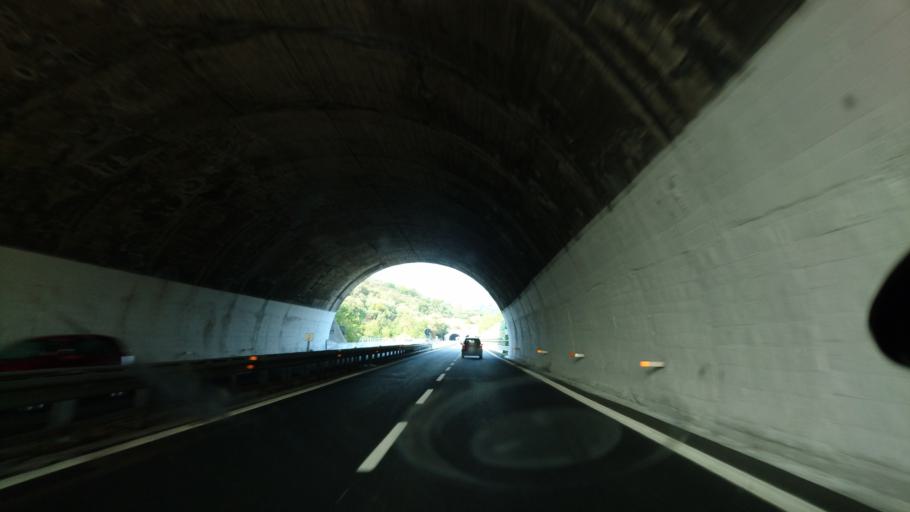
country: IT
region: Liguria
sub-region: Provincia di Savona
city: Savona
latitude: 44.3099
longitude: 8.4665
